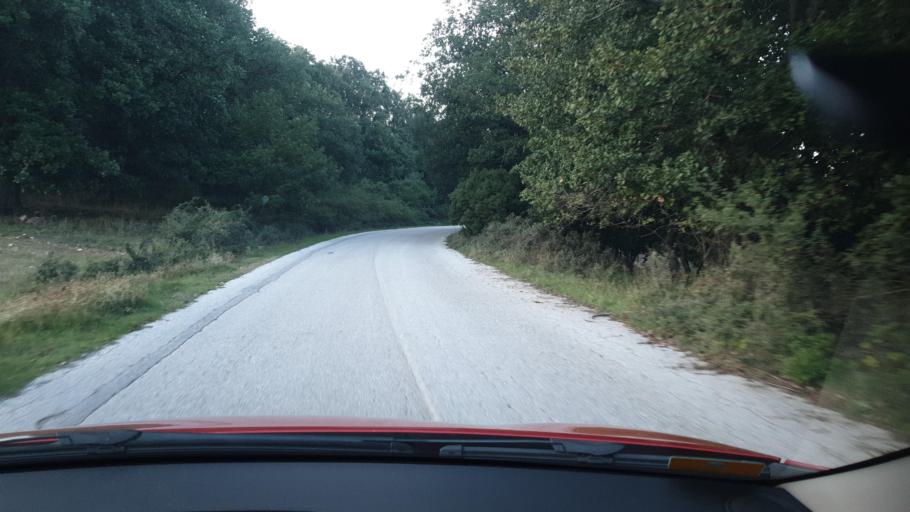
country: GR
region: Central Macedonia
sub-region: Nomos Thessalonikis
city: Peristera
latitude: 40.5140
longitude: 23.2143
